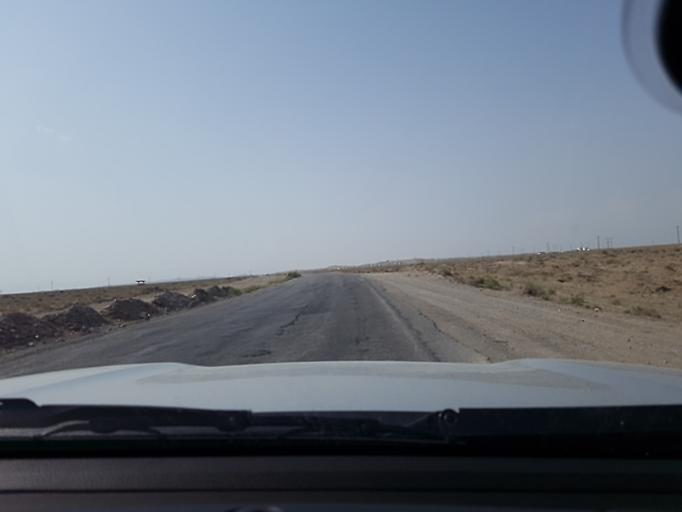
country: TM
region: Balkan
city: Gumdag
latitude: 39.2526
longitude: 54.5450
